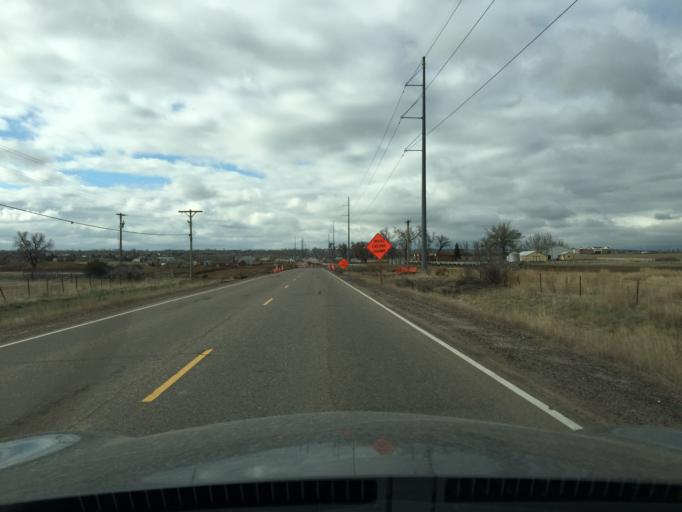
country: US
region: Colorado
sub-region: Adams County
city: Northglenn
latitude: 39.9639
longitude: -104.9784
